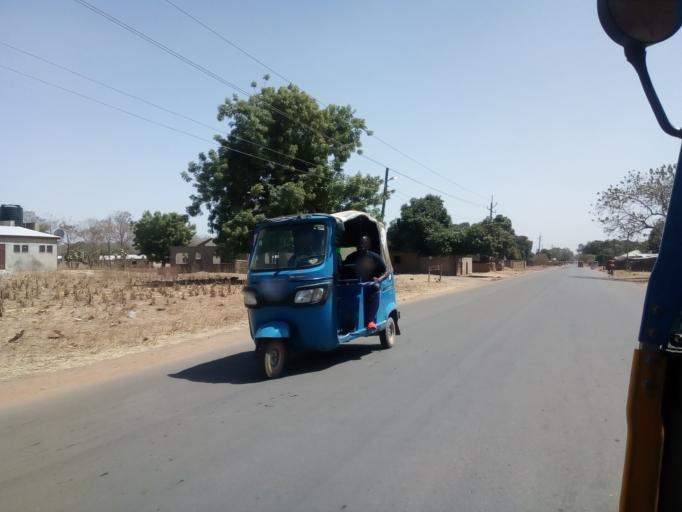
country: GH
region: Upper East
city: Navrongo
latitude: 10.8790
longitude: -1.0830
